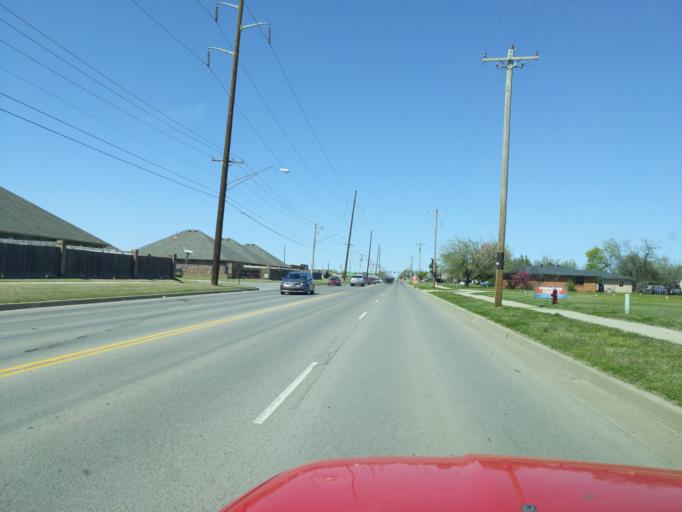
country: US
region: Oklahoma
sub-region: Cleveland County
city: Moore
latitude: 35.3306
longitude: -97.5120
